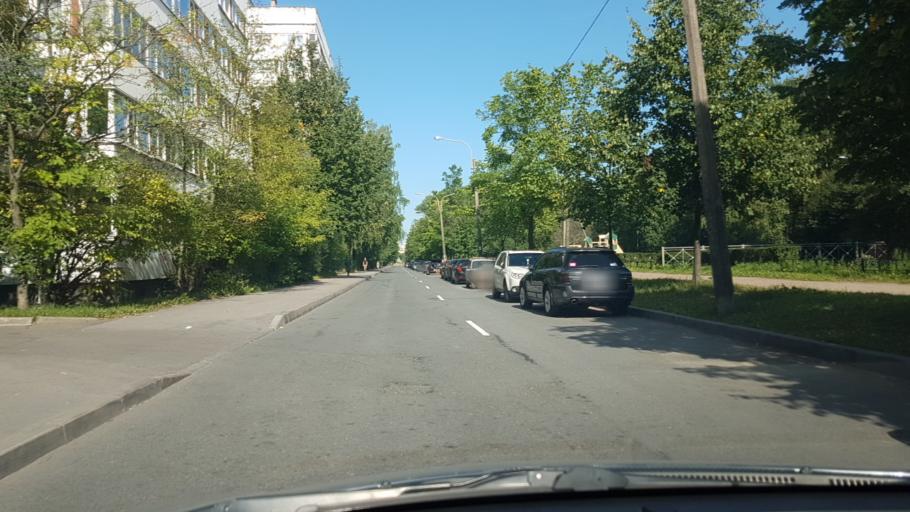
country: RU
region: St.-Petersburg
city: Dachnoye
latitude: 59.8375
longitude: 30.2201
